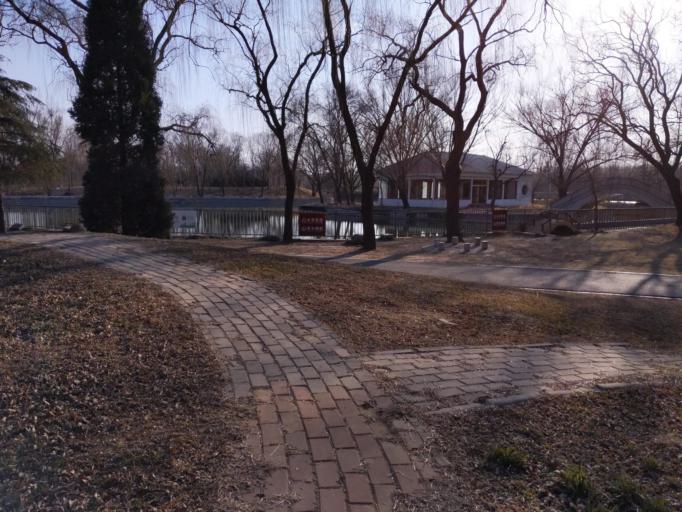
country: CN
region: Henan Sheng
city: Puyang
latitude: 35.7783
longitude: 114.9583
